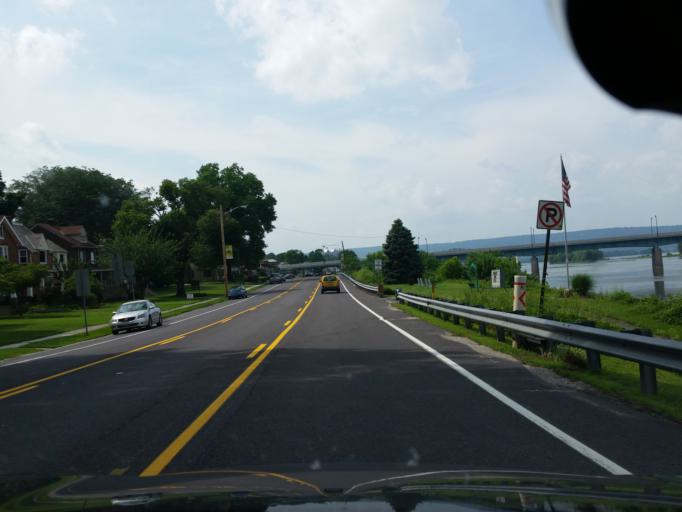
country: US
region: Pennsylvania
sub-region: Cumberland County
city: Wormleysburg
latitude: 40.2579
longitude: -76.9019
